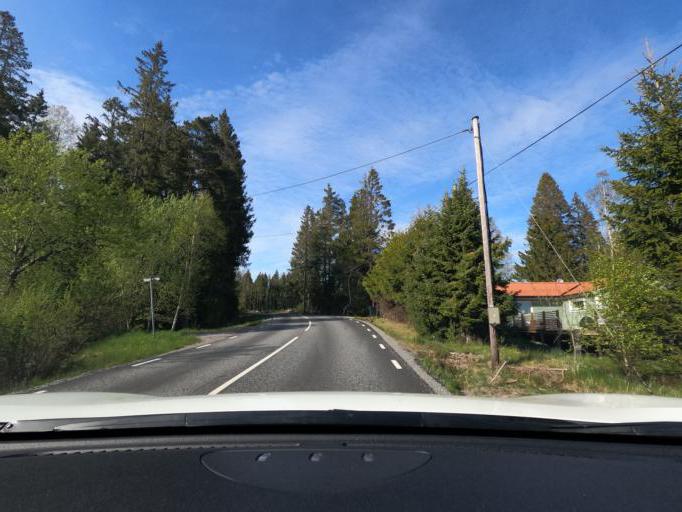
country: SE
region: Vaestra Goetaland
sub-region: Harryda Kommun
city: Landvetter
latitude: 57.6419
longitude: 12.2546
